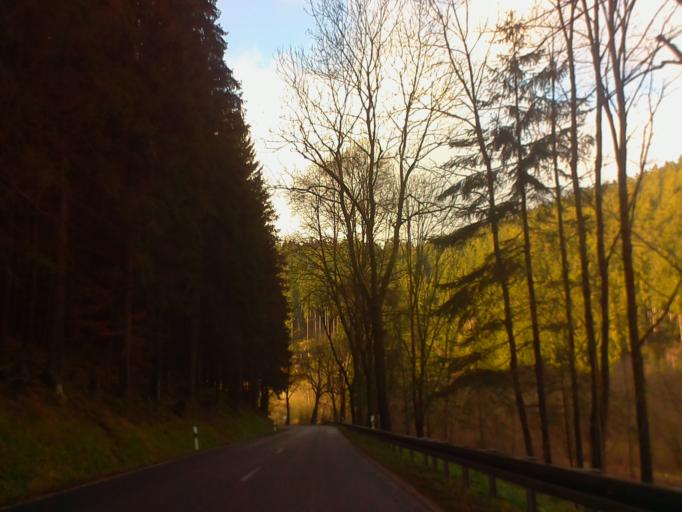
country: DE
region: Thuringia
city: Katzhutte
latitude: 50.5619
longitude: 11.0656
